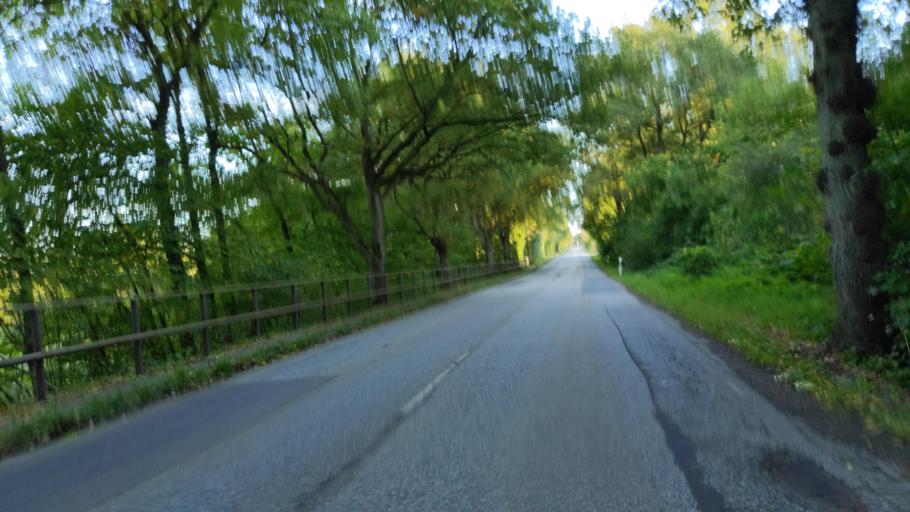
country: DE
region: Schleswig-Holstein
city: Susel
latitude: 54.0858
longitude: 10.6919
